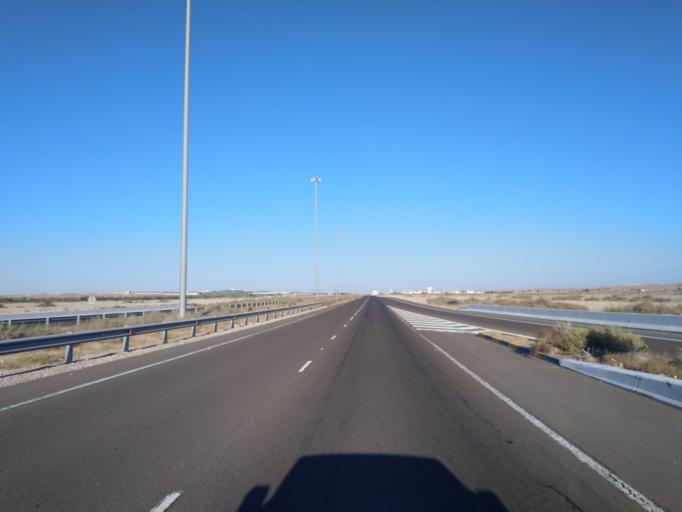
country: OM
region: Al Buraimi
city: Al Buraymi
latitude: 24.5032
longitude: 55.4524
